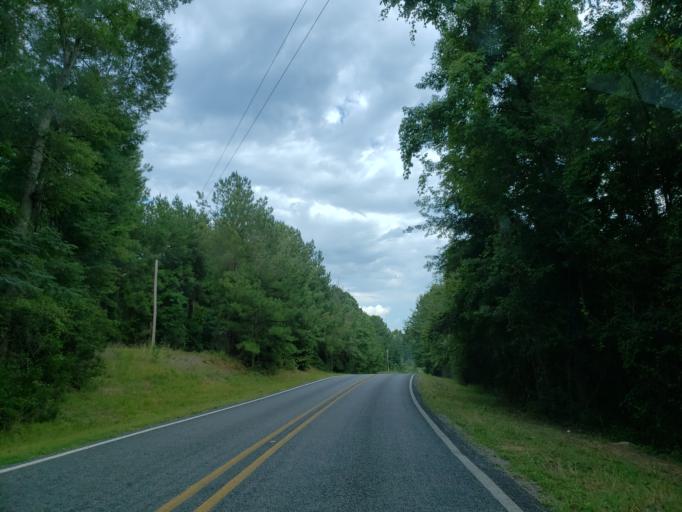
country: US
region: Mississippi
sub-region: Clarke County
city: Stonewall
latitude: 32.1772
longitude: -88.9161
